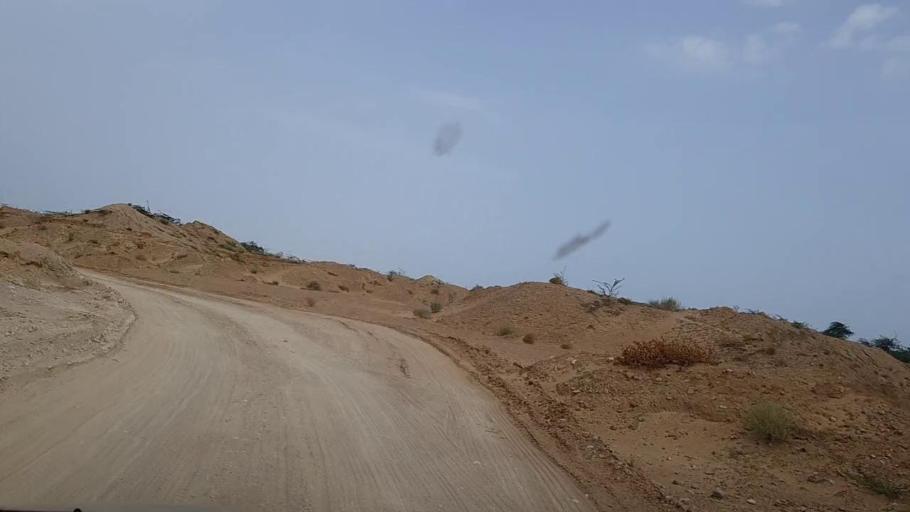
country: PK
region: Sindh
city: Kotri
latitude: 25.2820
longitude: 68.2615
